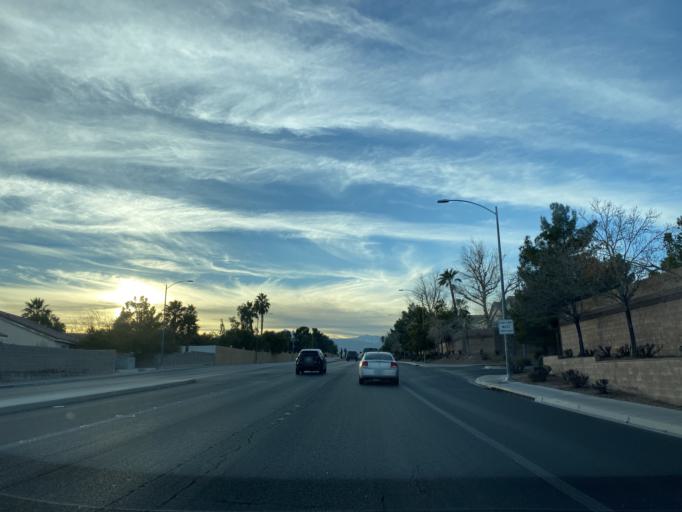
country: US
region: Nevada
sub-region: Clark County
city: North Las Vegas
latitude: 36.2616
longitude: -115.2092
